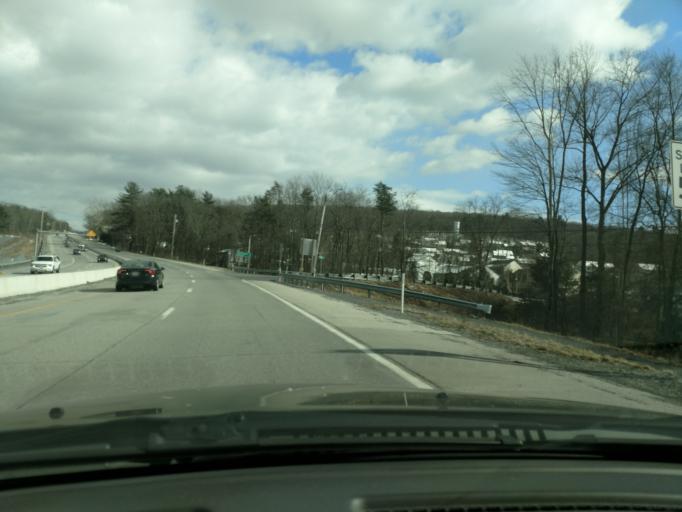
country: US
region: Pennsylvania
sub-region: Schuylkill County
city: Orwigsburg
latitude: 40.6186
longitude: -76.0567
